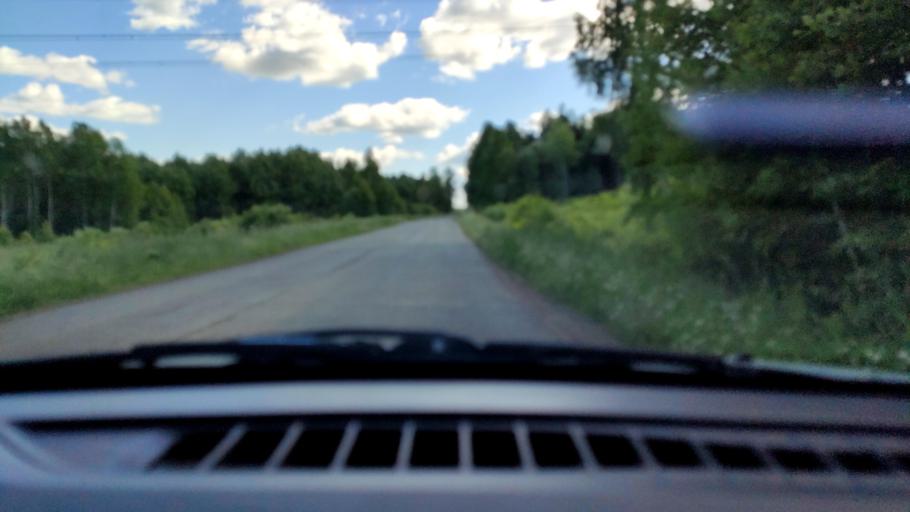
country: RU
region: Perm
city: Uinskoye
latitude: 57.1534
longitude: 56.5716
